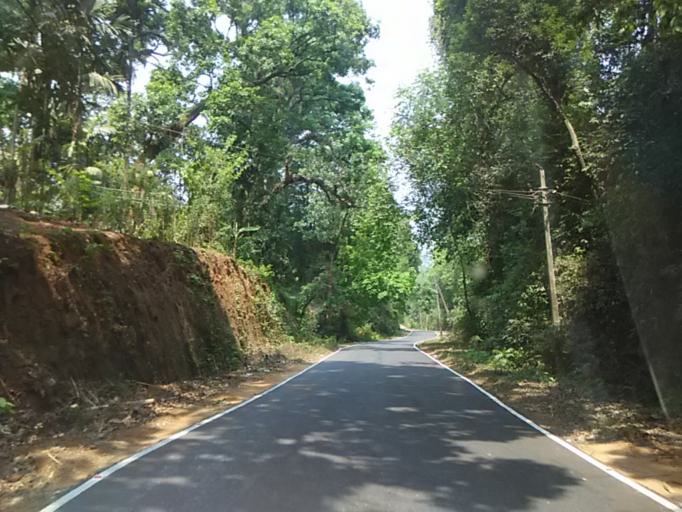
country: IN
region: Karnataka
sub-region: Kodagu
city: Virarajendrapet
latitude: 12.0733
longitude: 75.7274
